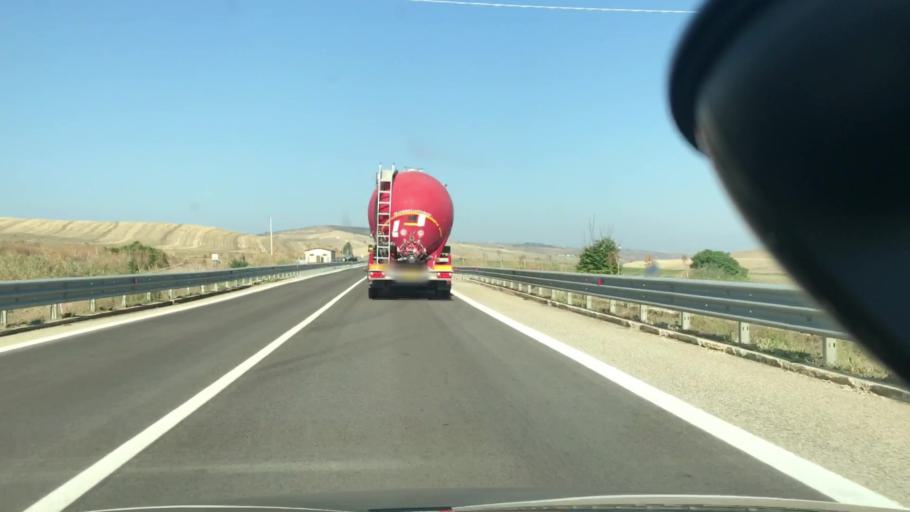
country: IT
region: Basilicate
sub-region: Provincia di Matera
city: Irsina
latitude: 40.7852
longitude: 16.2985
